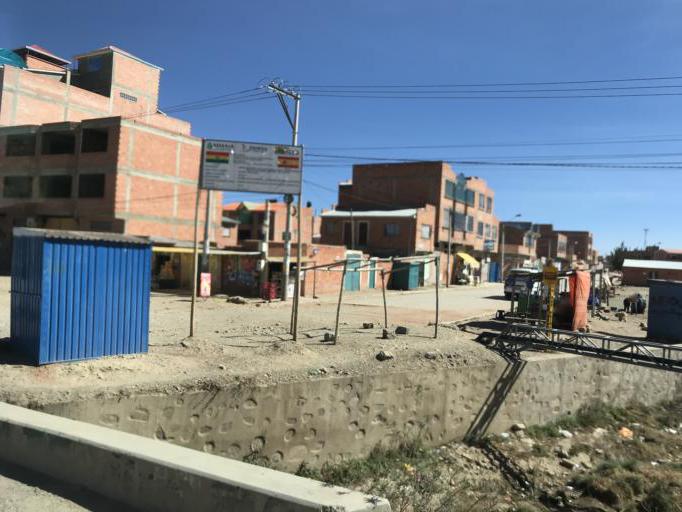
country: BO
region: La Paz
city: La Paz
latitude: -16.5052
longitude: -68.2530
